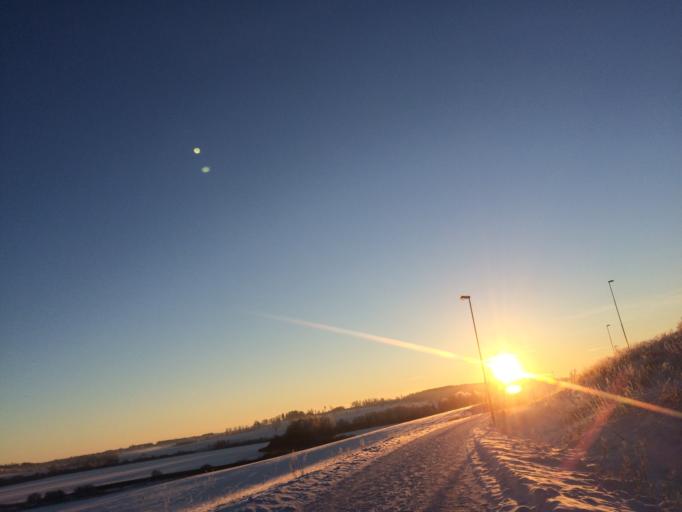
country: NO
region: Akershus
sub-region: Ski
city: Ski
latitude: 59.6958
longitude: 10.8317
